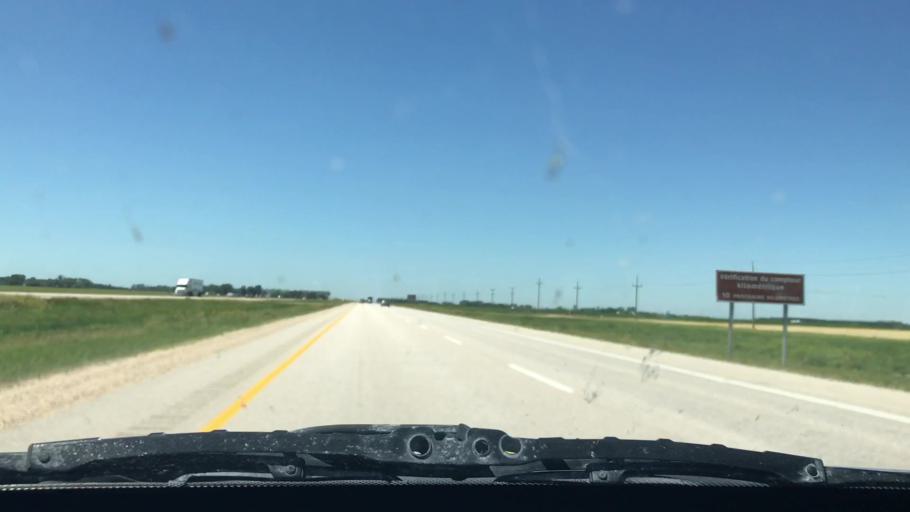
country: CA
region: Manitoba
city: Steinbach
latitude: 49.7245
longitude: -96.7044
